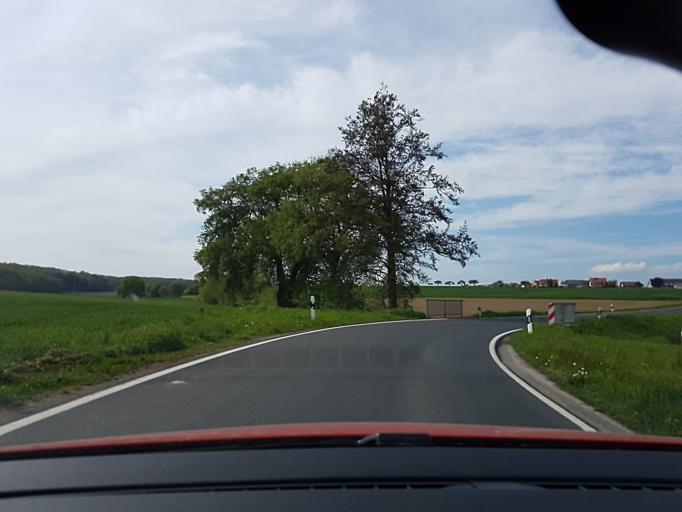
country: DE
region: Bavaria
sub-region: Regierungsbezirk Unterfranken
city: Unterpleichfeld
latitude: 49.9027
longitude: 10.0197
